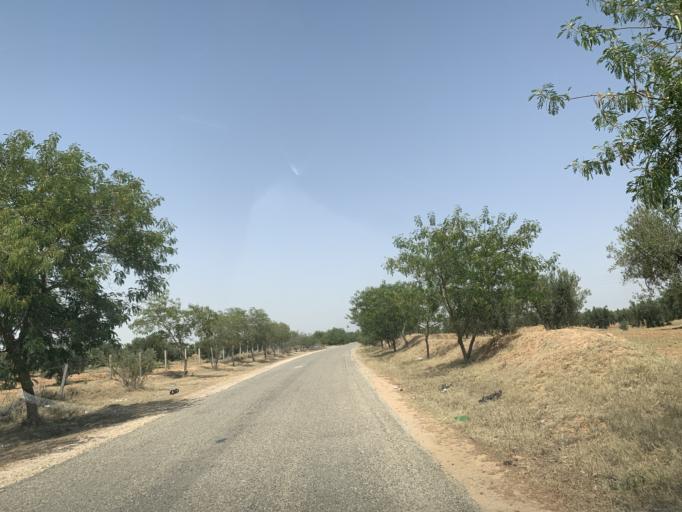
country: TN
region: Al Mahdiyah
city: Shurban
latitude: 35.1929
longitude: 10.2507
